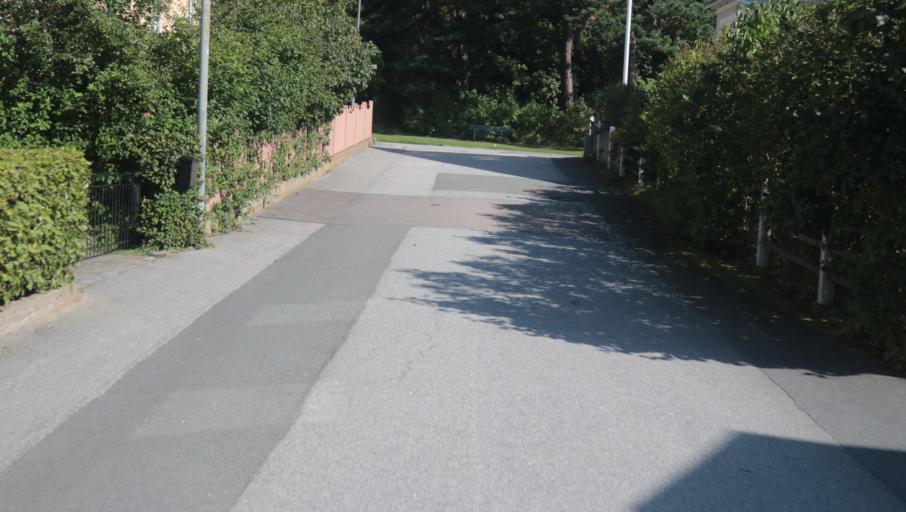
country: SE
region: Blekinge
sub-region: Karlshamns Kommun
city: Karlshamn
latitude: 56.1765
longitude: 14.8601
